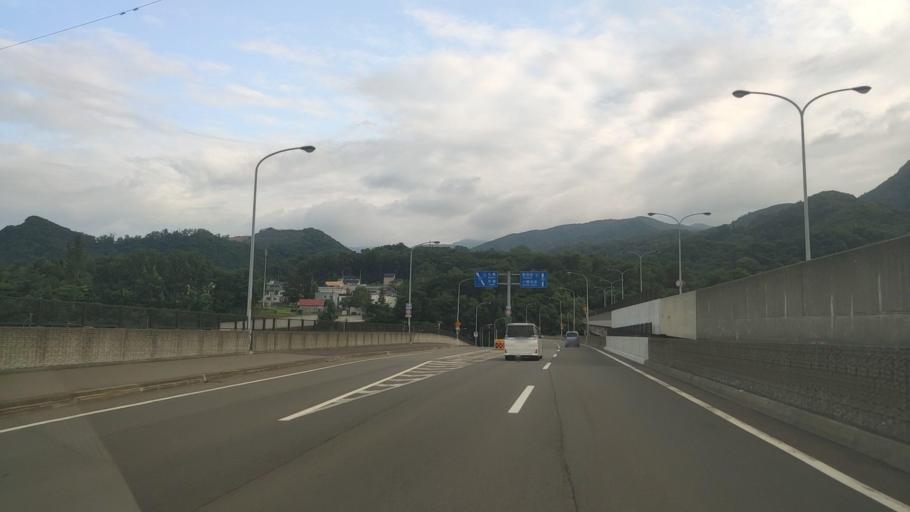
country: JP
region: Hokkaido
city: Otaru
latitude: 43.1370
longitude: 141.1781
